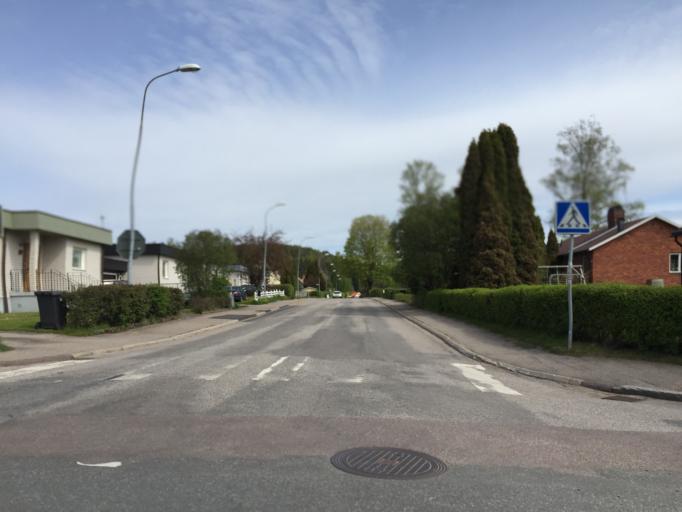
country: SE
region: Dalarna
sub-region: Ludvika Kommun
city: Ludvika
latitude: 60.1258
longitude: 15.1855
